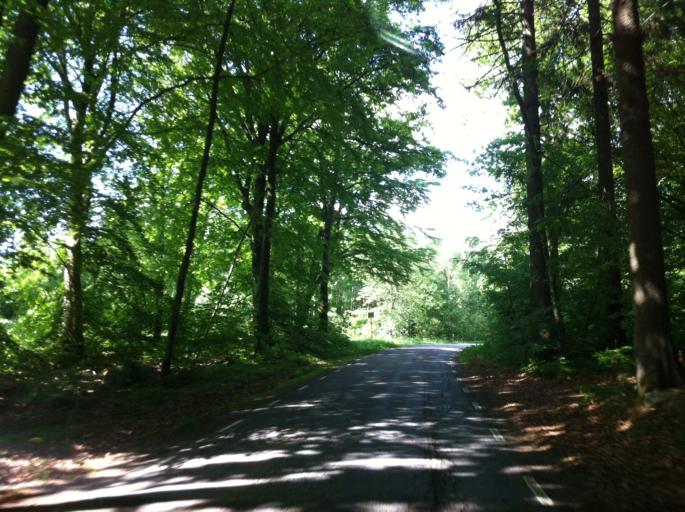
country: SE
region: Skane
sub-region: Svalovs Kommun
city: Kagerod
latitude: 56.0241
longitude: 13.1613
